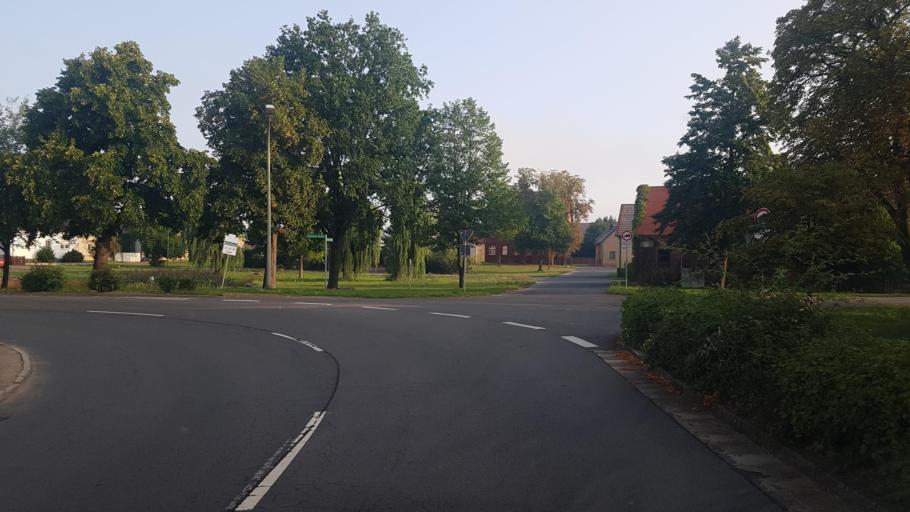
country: DE
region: Saxony-Anhalt
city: Prettin
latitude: 51.7013
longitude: 12.8870
